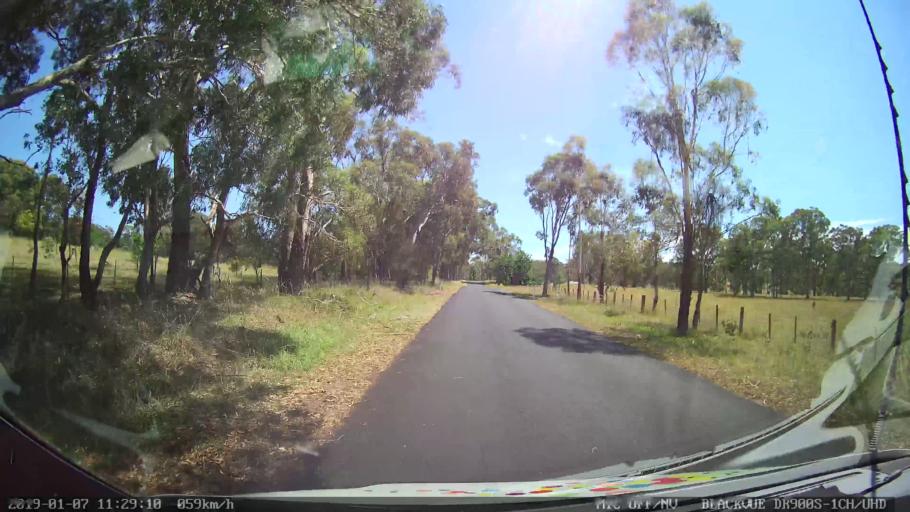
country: AU
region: New South Wales
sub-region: Armidale Dumaresq
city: Armidale
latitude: -30.4413
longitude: 151.5649
